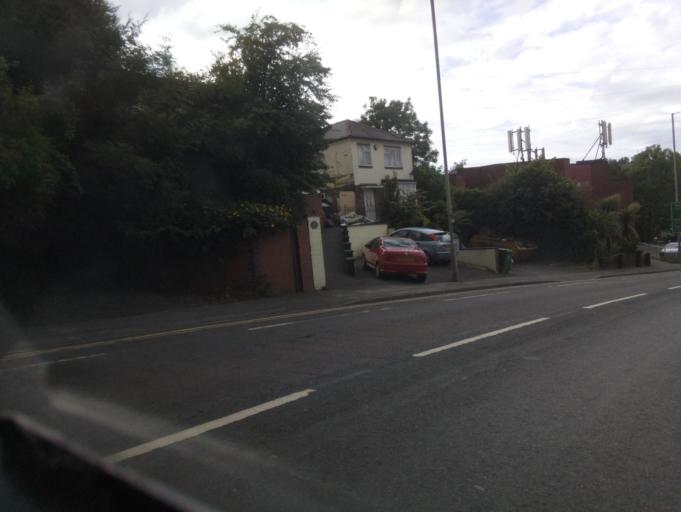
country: GB
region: England
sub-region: Worcestershire
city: Kidderminster
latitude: 52.3979
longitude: -2.2372
